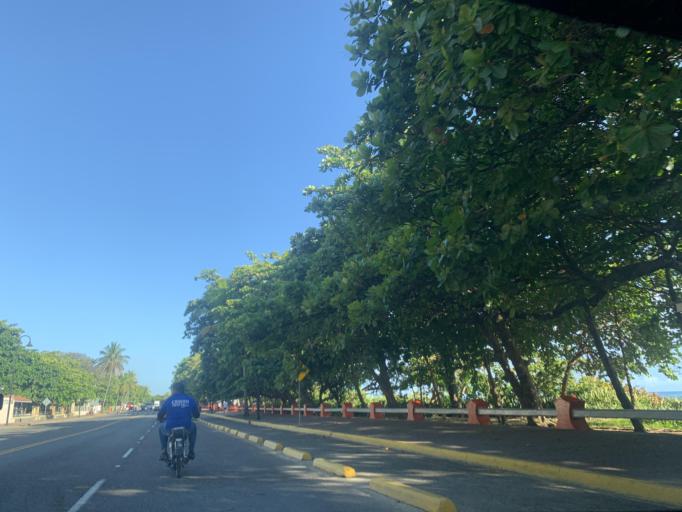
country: DO
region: Puerto Plata
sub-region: Puerto Plata
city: Puerto Plata
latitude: 19.7909
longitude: -70.6728
